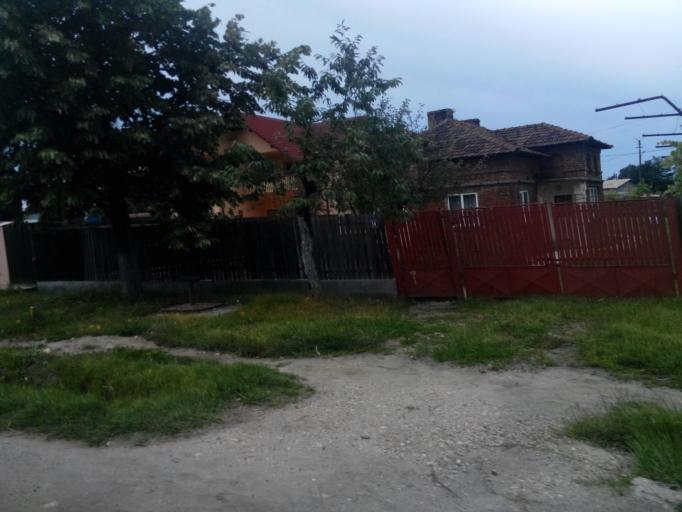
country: RO
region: Arges
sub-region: Comuna Bascov
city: Bascov
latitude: 44.8939
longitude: 24.8199
